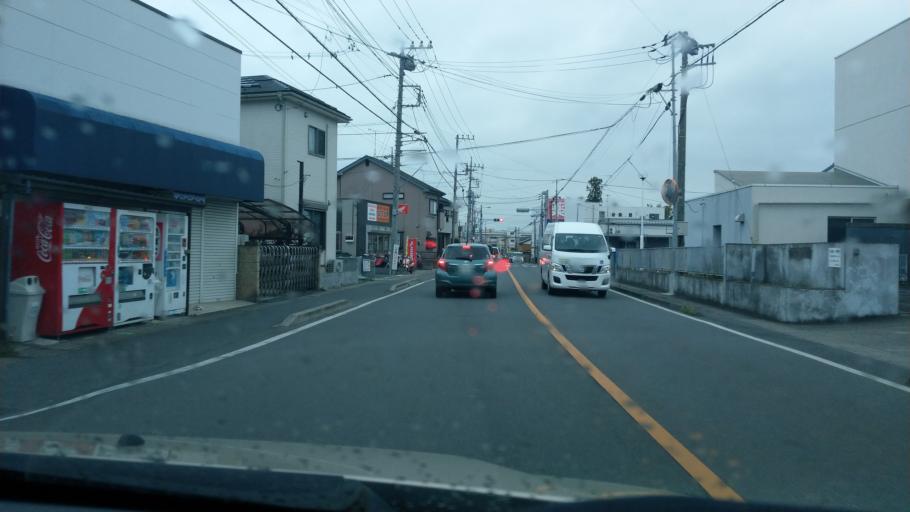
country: JP
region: Saitama
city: Iwatsuki
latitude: 35.9317
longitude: 139.6733
